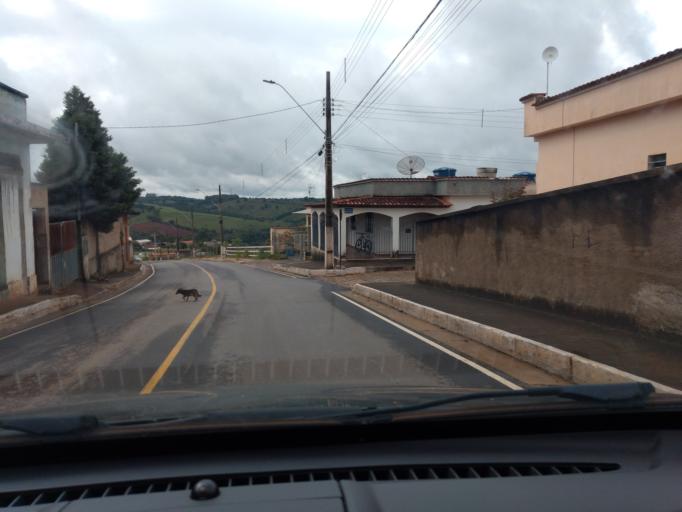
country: BR
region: Minas Gerais
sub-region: Lavras
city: Lavras
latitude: -21.5090
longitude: -44.9078
